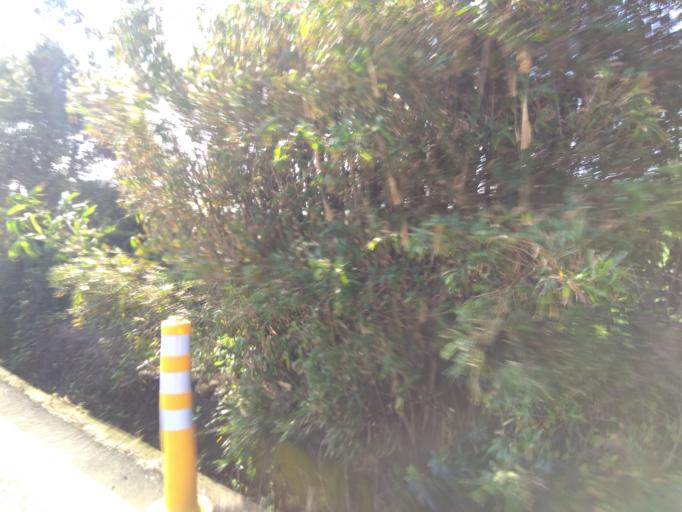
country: TW
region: Taiwan
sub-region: Hsinchu
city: Zhubei
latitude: 24.9580
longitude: 121.0038
